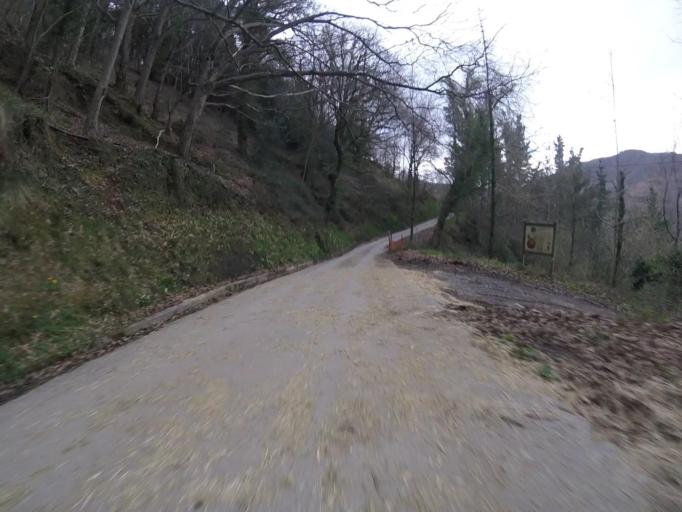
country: ES
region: Basque Country
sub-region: Provincia de Guipuzcoa
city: Errenteria
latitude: 43.2738
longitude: -1.8603
